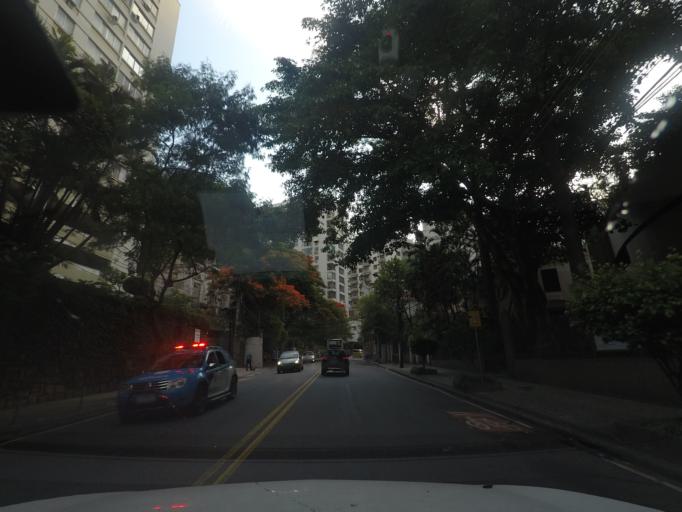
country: BR
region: Rio de Janeiro
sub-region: Rio De Janeiro
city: Rio de Janeiro
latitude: -22.9402
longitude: -43.1967
